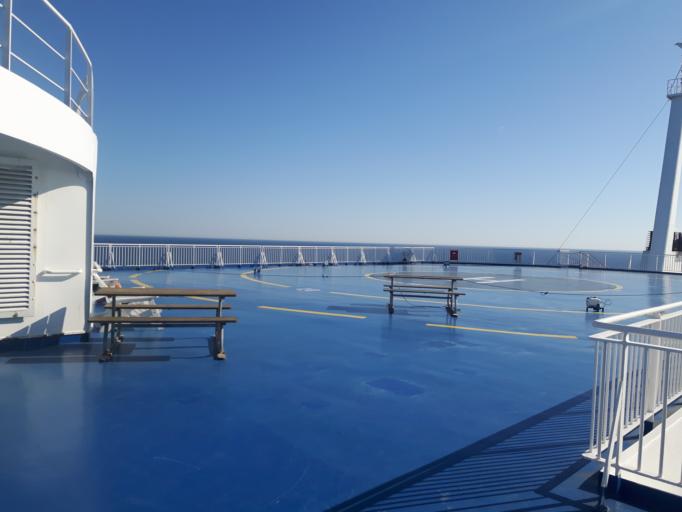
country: SE
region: Gotland
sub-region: Gotland
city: Hemse
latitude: 56.5983
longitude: 17.9617
